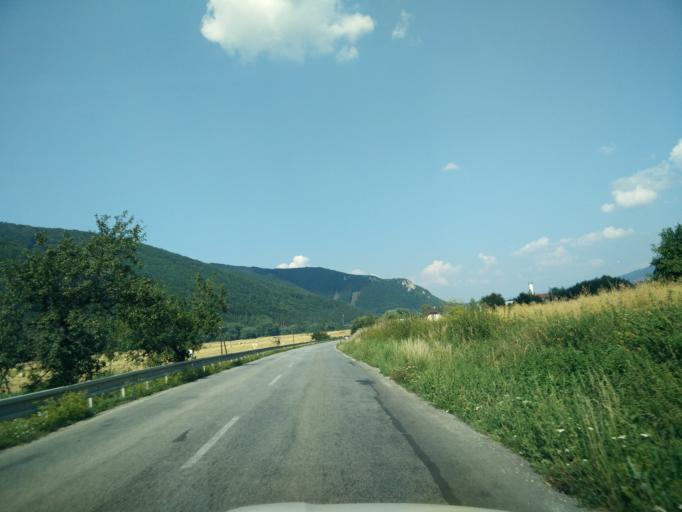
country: SK
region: Zilinsky
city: Rajec
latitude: 49.1211
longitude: 18.6629
